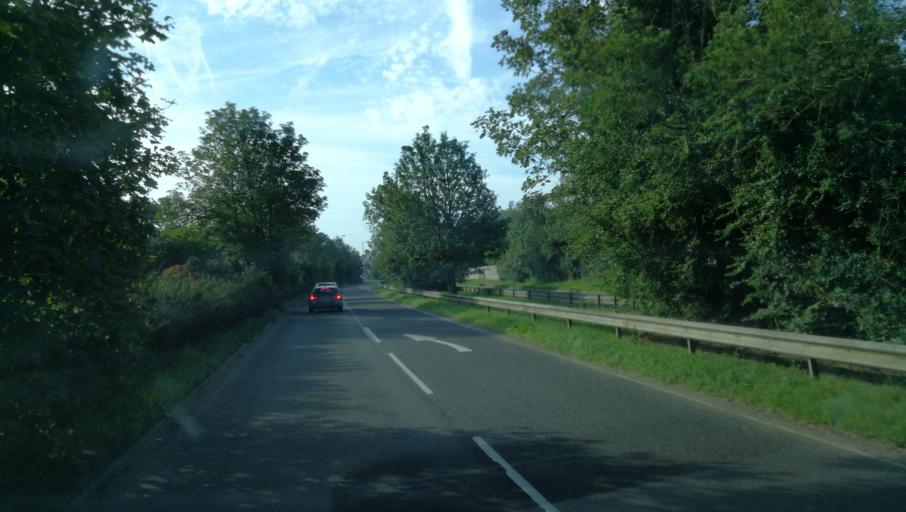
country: GB
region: England
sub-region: Oxfordshire
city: Yarnton
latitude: 51.8246
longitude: -1.3194
